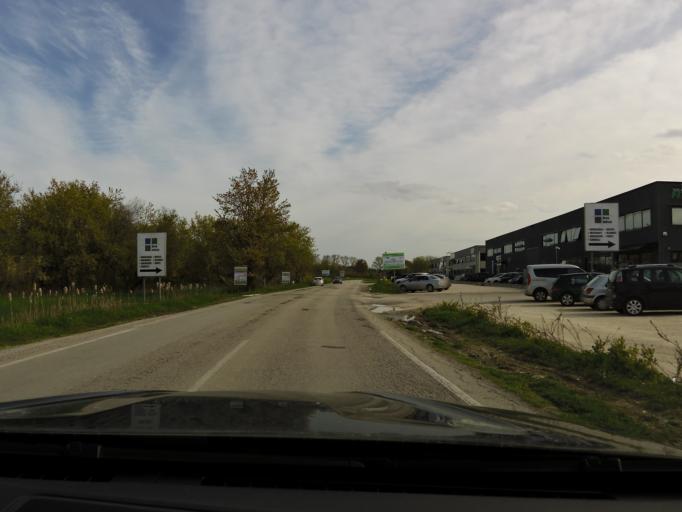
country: IT
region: The Marches
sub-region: Provincia di Ancona
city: Camerano
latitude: 43.5244
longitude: 13.5248
